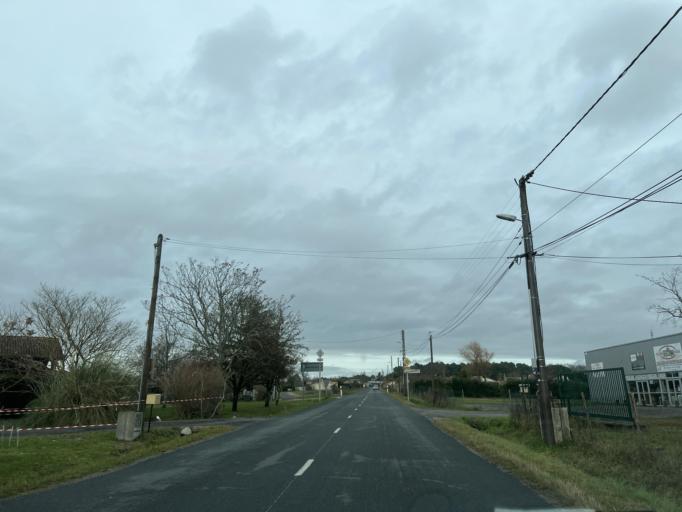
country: FR
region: Aquitaine
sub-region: Departement de la Gironde
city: Saint-Ciers-sur-Gironde
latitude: 45.2791
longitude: -0.6127
